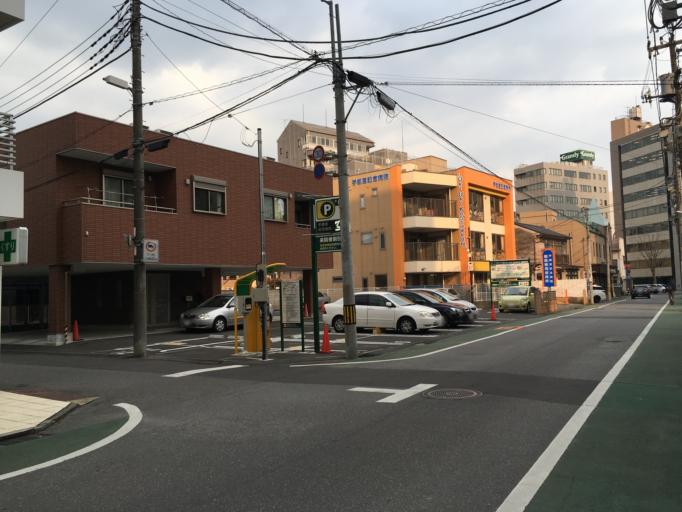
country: JP
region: Tochigi
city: Utsunomiya-shi
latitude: 36.5608
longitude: 139.8927
